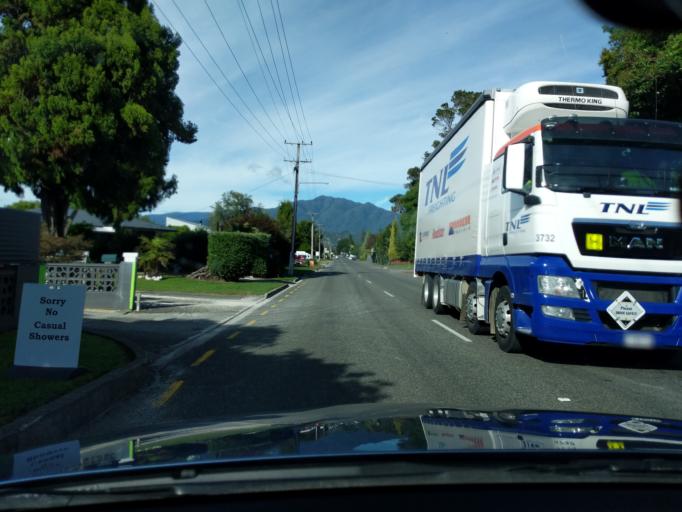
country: NZ
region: Tasman
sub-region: Tasman District
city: Takaka
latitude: -40.8580
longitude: 172.8104
